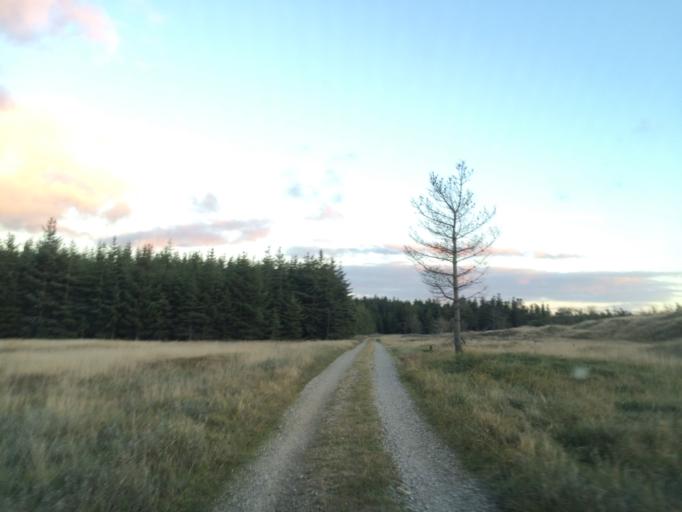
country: DK
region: Central Jutland
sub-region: Holstebro Kommune
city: Ulfborg
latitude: 56.2989
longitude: 8.1490
